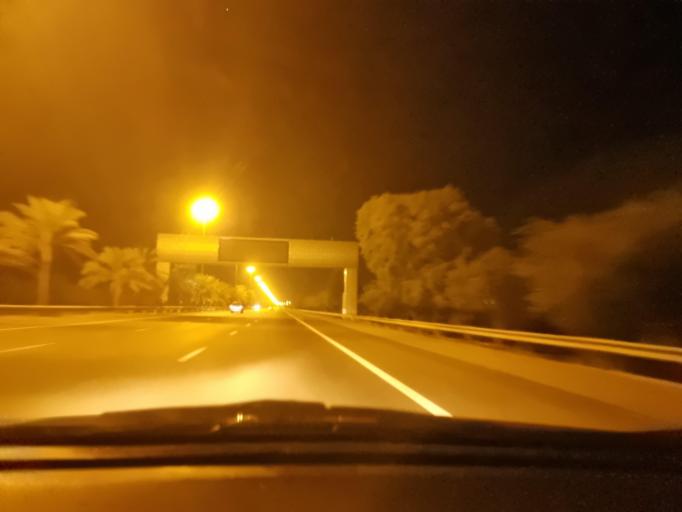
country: AE
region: Abu Dhabi
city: Al Ain
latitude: 24.1962
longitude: 55.3613
